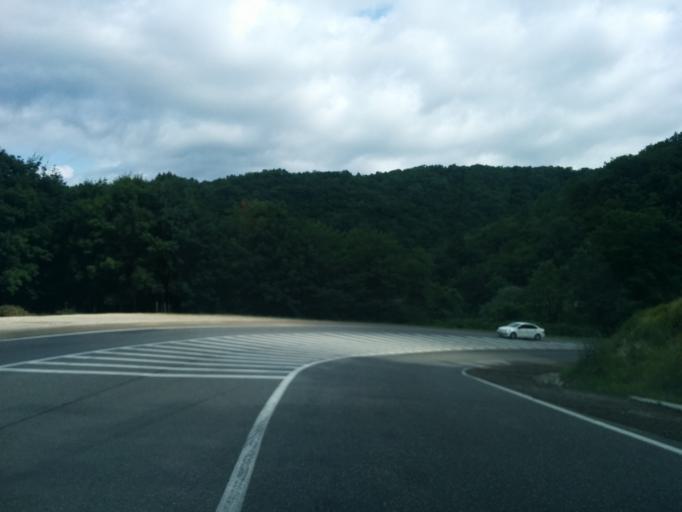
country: RU
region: Krasnodarskiy
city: Agoy
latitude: 44.1419
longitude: 39.0557
